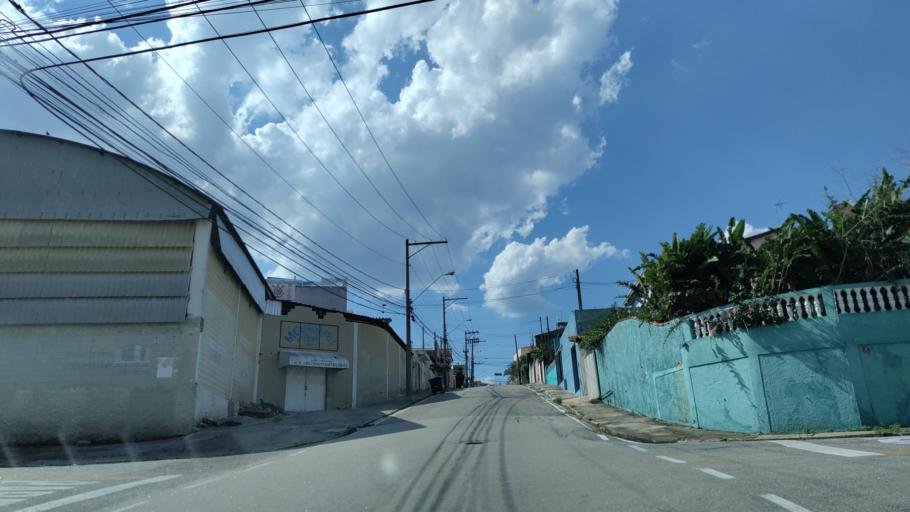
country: BR
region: Sao Paulo
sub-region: Sorocaba
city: Sorocaba
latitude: -23.4805
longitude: -47.4457
